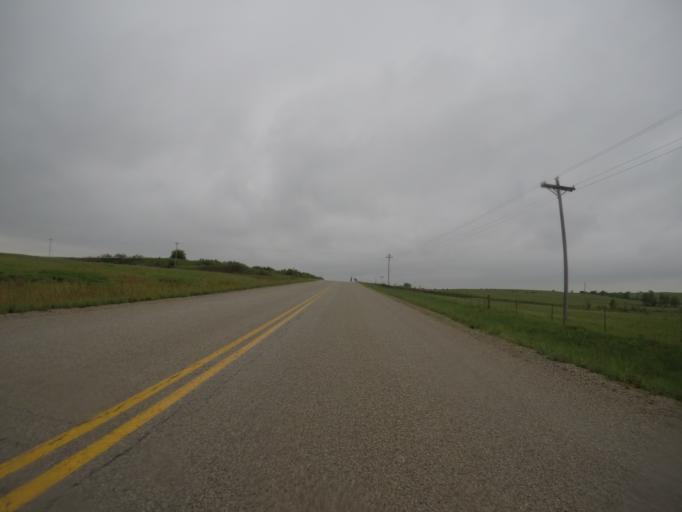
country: US
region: Kansas
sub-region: Pottawatomie County
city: Westmoreland
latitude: 39.3770
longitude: -96.2202
